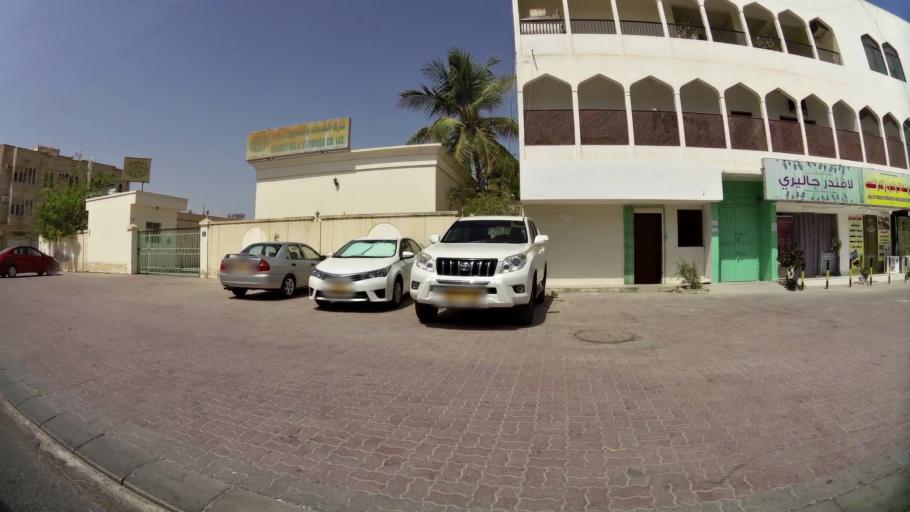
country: OM
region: Zufar
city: Salalah
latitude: 17.0107
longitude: 54.0731
